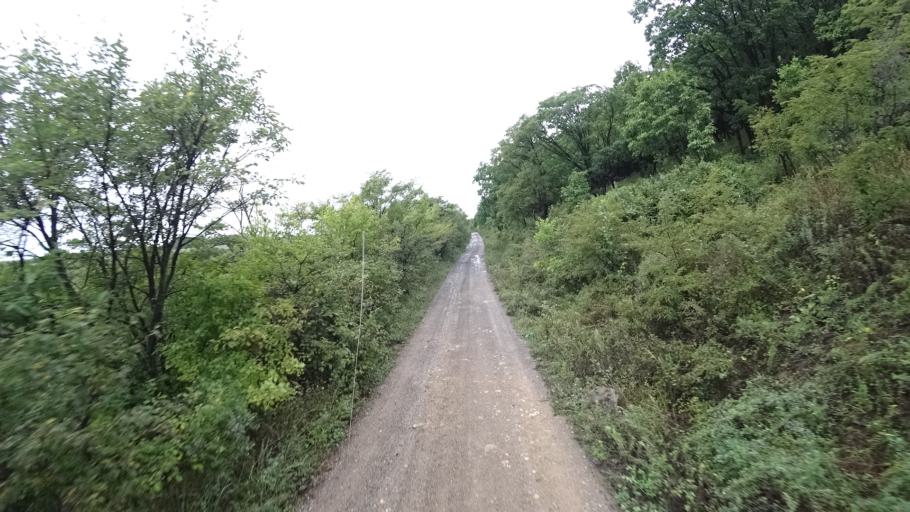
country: RU
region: Primorskiy
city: Monastyrishche
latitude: 44.2594
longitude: 132.4083
